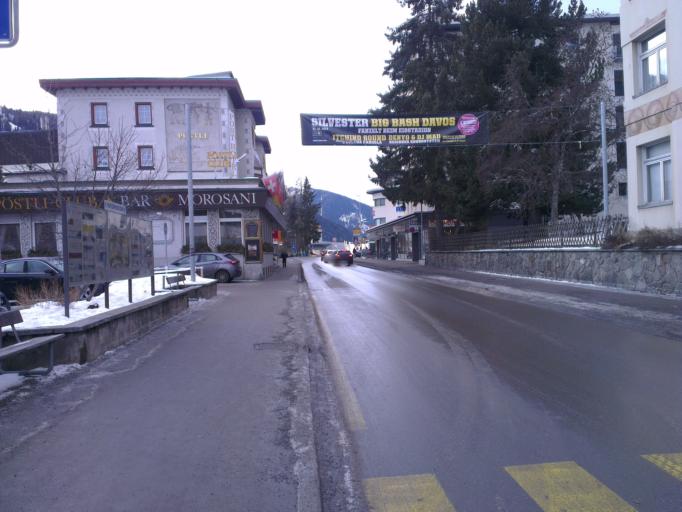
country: CH
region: Grisons
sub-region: Praettigau/Davos District
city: Davos
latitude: 46.7944
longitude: 9.8210
